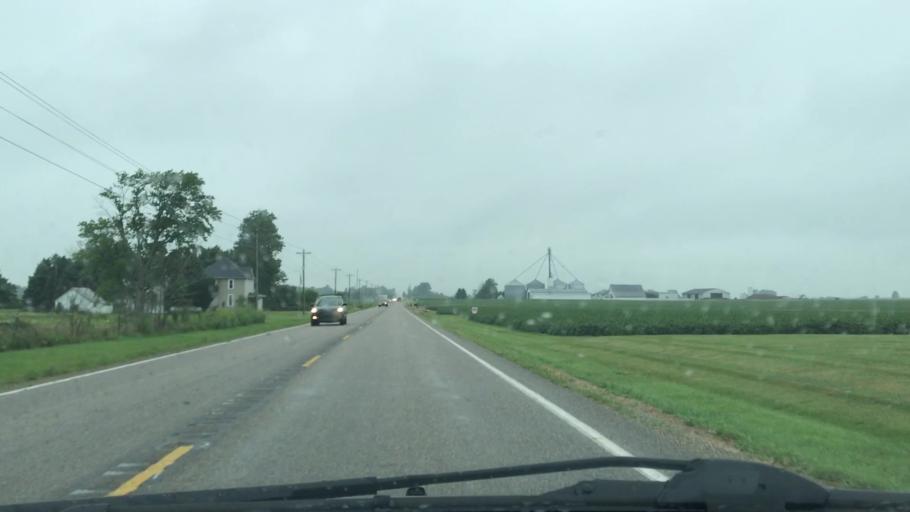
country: US
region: Indiana
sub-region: Boone County
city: Lebanon
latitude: 40.1263
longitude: -86.4645
